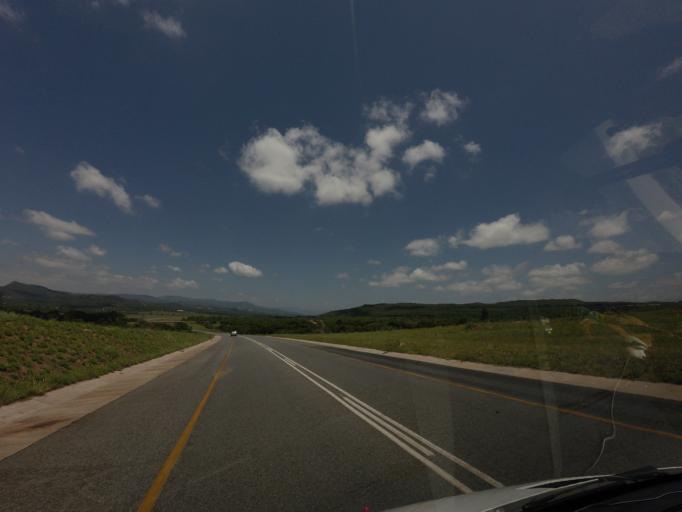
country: ZA
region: Mpumalanga
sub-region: Ehlanzeni District
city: Nelspruit
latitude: -25.4388
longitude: 30.9435
